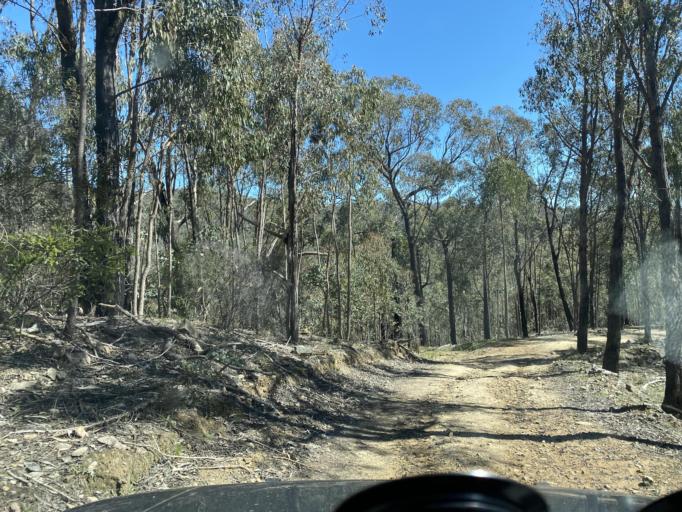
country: AU
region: Victoria
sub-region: Benalla
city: Benalla
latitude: -36.7189
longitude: 146.1810
